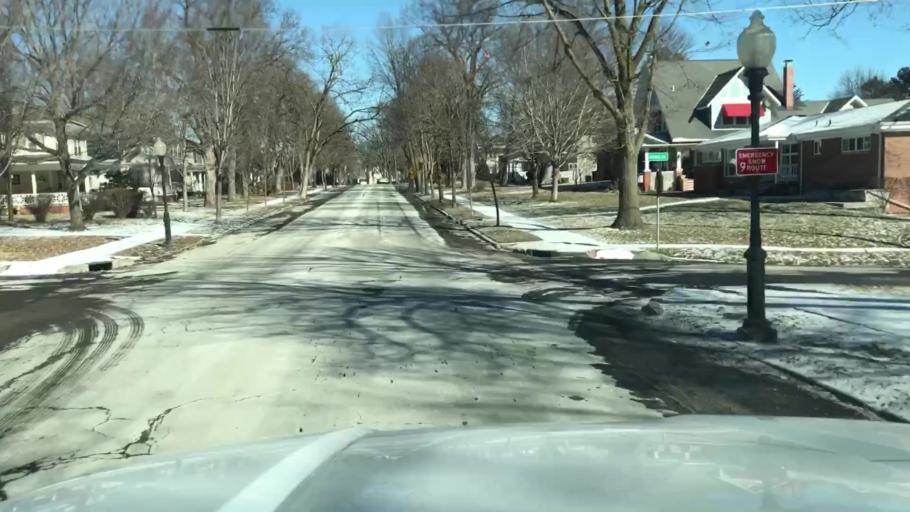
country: US
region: Missouri
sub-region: Buchanan County
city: Saint Joseph
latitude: 39.7824
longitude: -94.8239
